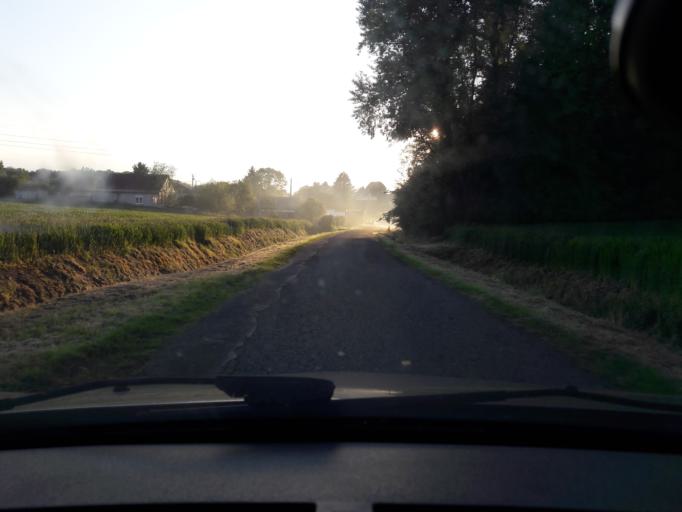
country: FR
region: Nord-Pas-de-Calais
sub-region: Departement du Nord
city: Recquignies
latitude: 50.2763
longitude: 4.0506
